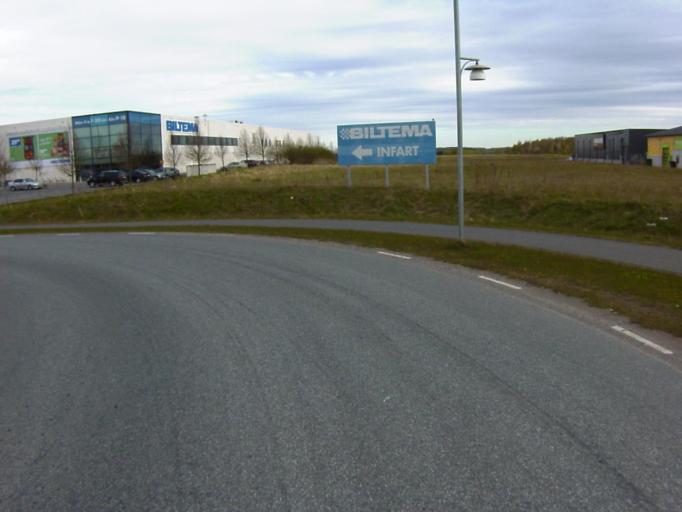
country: SE
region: Skane
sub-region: Kristianstads Kommun
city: Kristianstad
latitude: 56.0223
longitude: 14.1156
